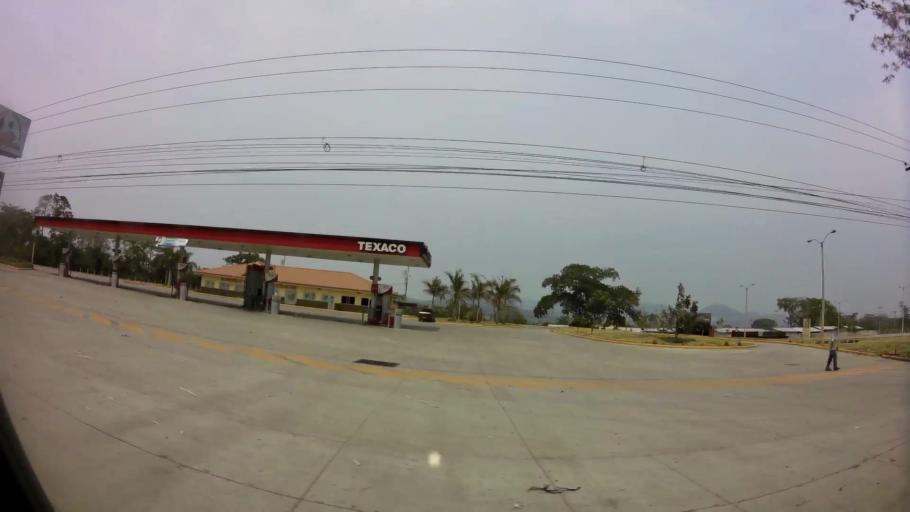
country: HN
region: Cortes
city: Villanueva
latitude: 15.3522
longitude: -87.9841
